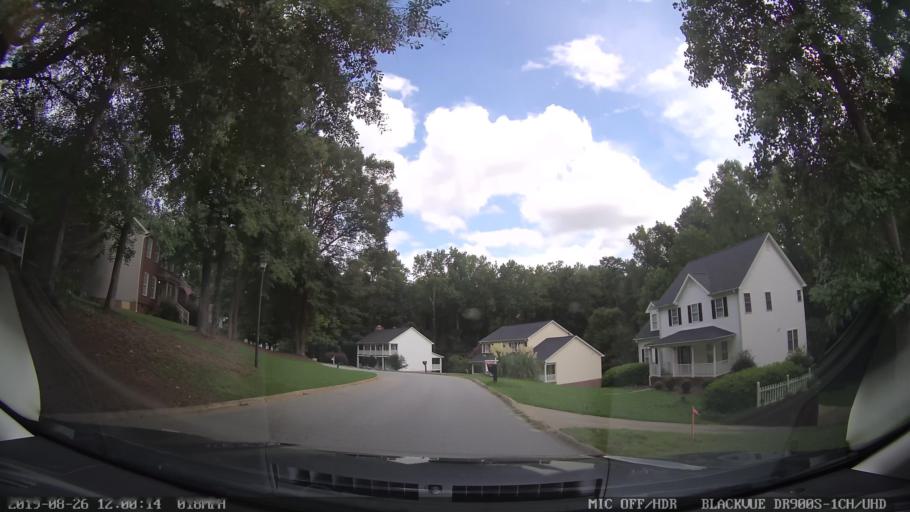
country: US
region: South Carolina
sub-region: Greenville County
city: Five Forks
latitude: 34.7998
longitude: -82.2342
